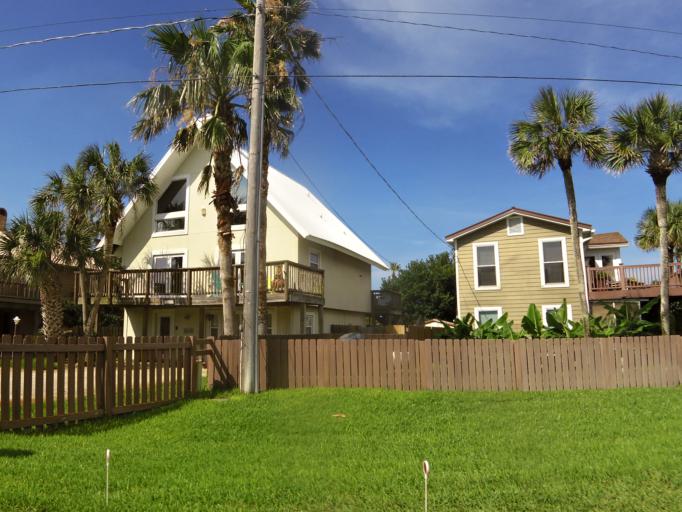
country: US
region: Florida
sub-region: Saint Johns County
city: Villano Beach
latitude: 29.9142
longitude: -81.2921
